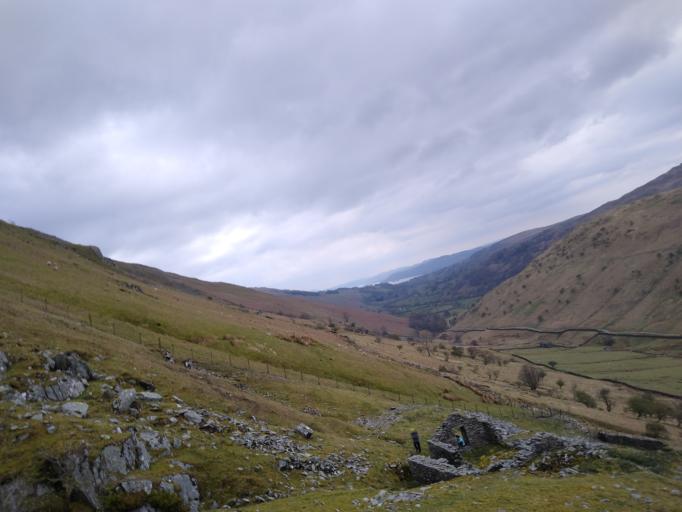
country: GB
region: England
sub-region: Cumbria
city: Windermere
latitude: 54.4546
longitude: -2.8812
